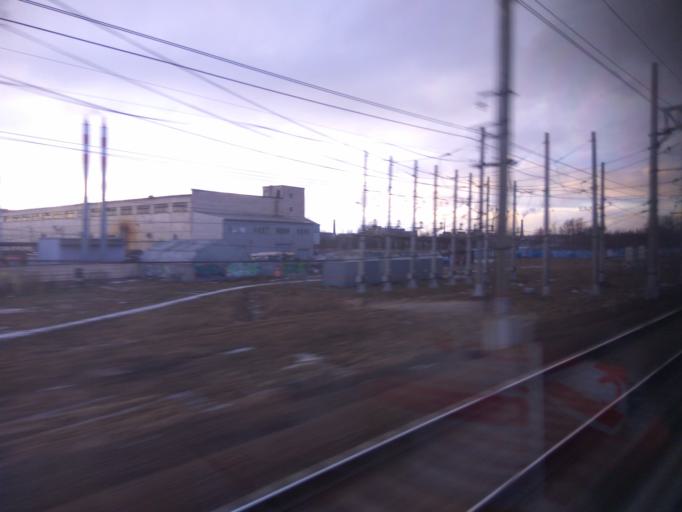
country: RU
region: St.-Petersburg
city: Centralniy
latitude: 59.8950
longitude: 30.3897
